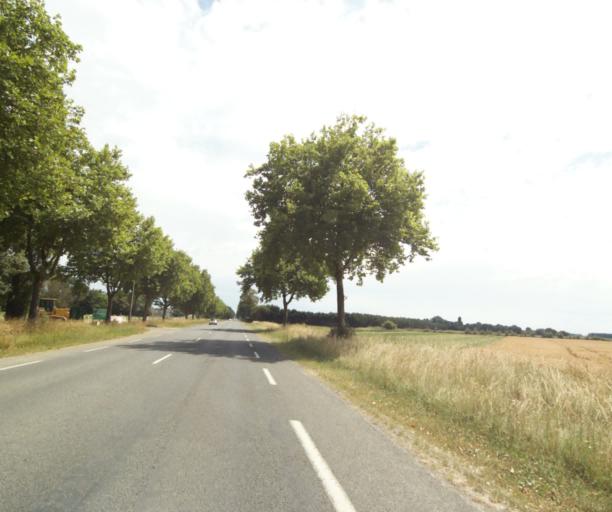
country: FR
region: Ile-de-France
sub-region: Departement de Seine-et-Marne
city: Chailly-en-Biere
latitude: 48.4757
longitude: 2.5992
